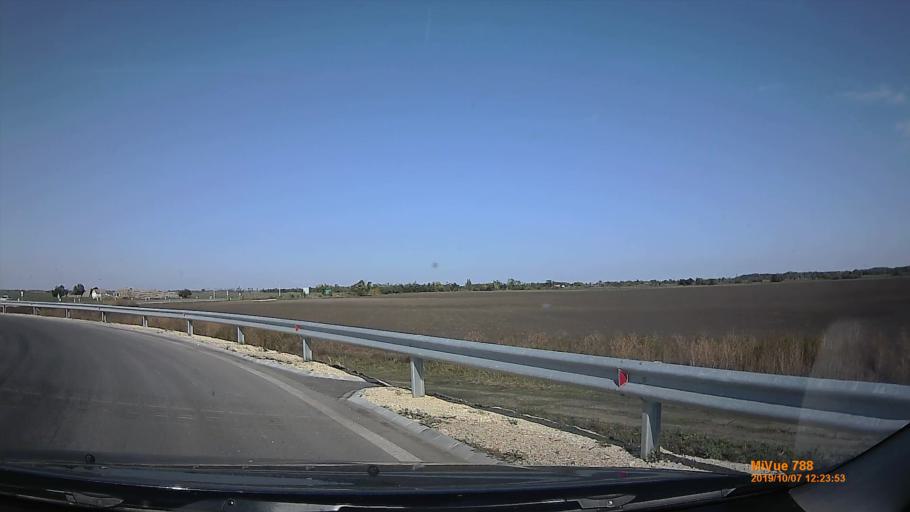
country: HU
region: Jasz-Nagykun-Szolnok
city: Kunszentmarton
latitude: 46.8739
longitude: 20.2666
